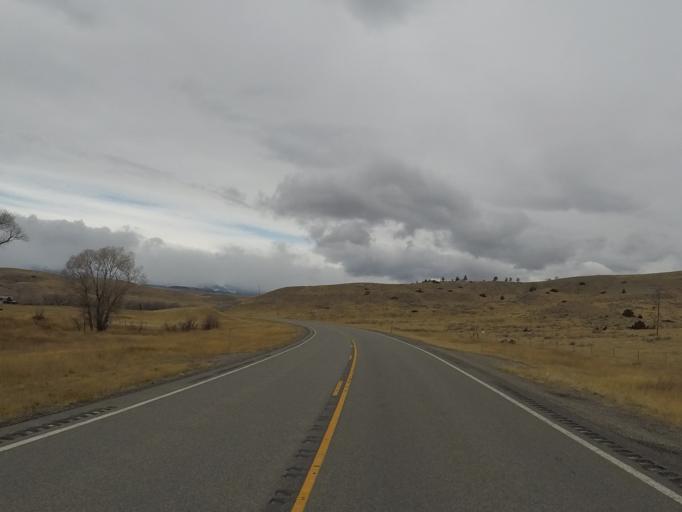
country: US
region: Montana
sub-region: Sweet Grass County
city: Big Timber
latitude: 45.8985
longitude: -109.9662
